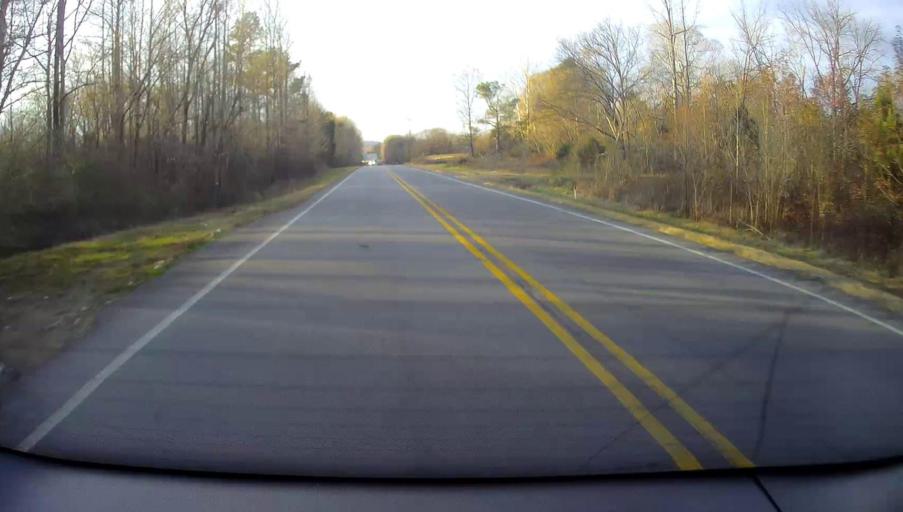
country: US
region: Alabama
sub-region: Blount County
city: Blountsville
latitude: 34.1549
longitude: -86.4589
